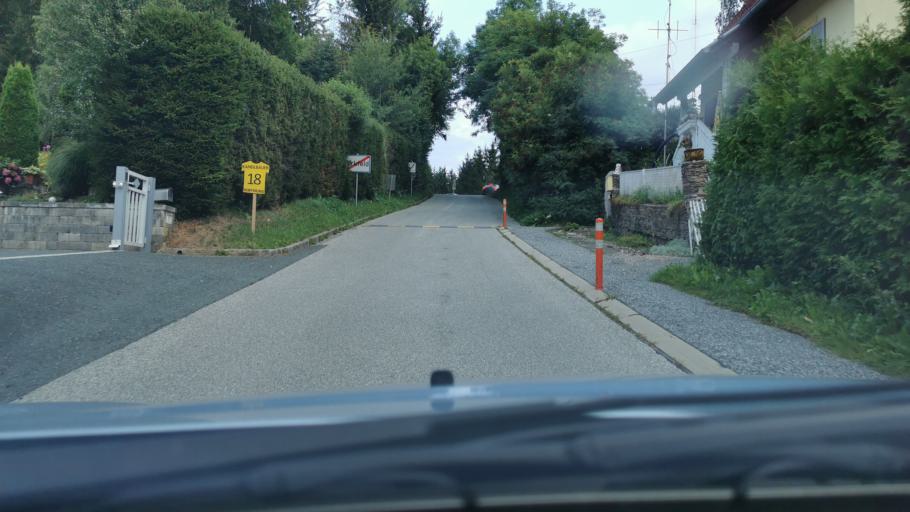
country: AT
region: Styria
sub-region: Politischer Bezirk Weiz
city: Birkfeld
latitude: 47.3617
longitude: 15.6894
